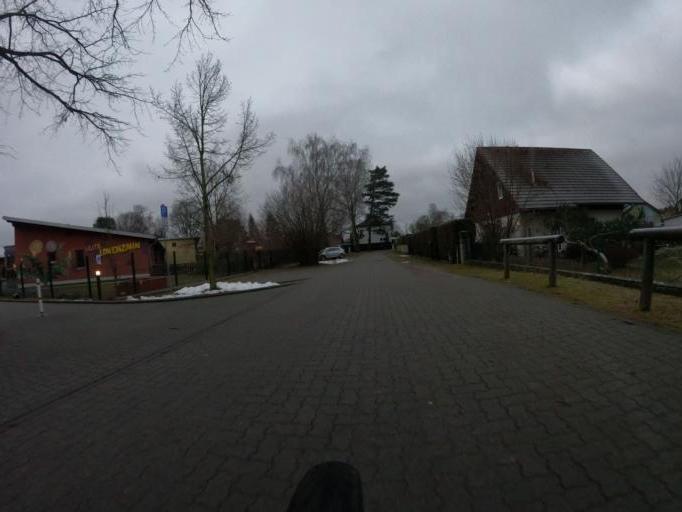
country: DE
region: Brandenburg
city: Schulzendorf
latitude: 52.3602
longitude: 13.5907
